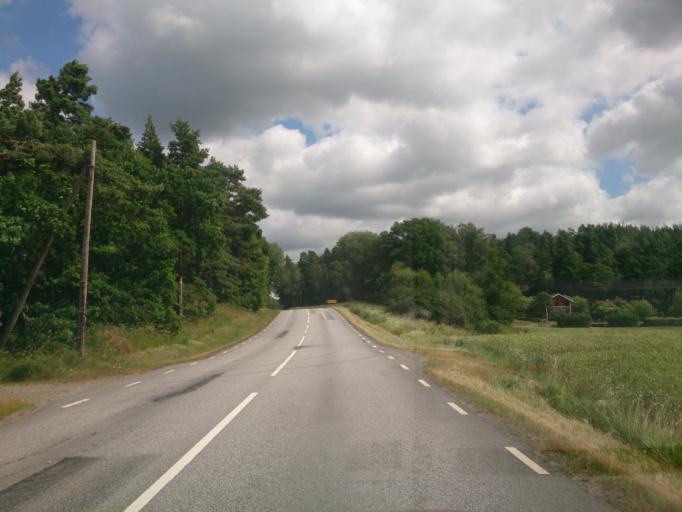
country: SE
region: OEstergoetland
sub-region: Soderkopings Kommun
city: Soederkoeping
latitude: 58.5004
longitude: 16.3157
